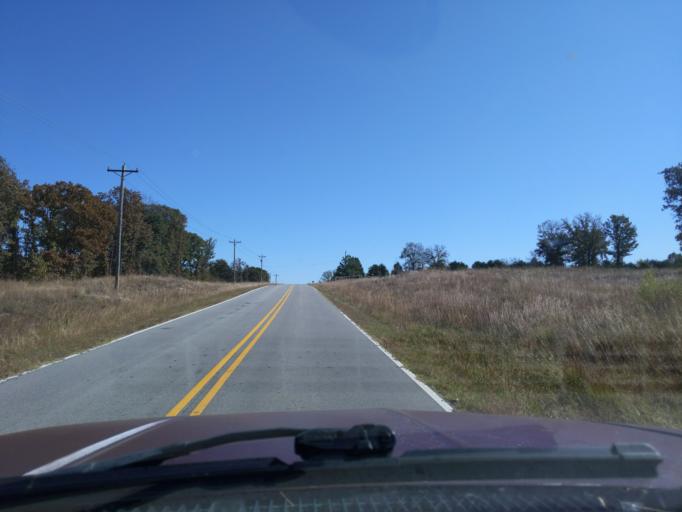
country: US
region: Oklahoma
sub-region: Creek County
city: Bristow
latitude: 35.7119
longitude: -96.3926
